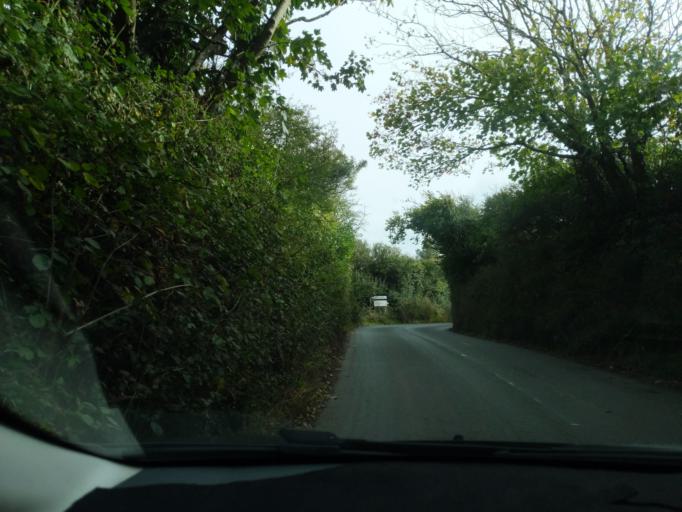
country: GB
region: England
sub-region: Cornwall
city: Mevagissey
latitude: 50.2456
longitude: -4.8068
